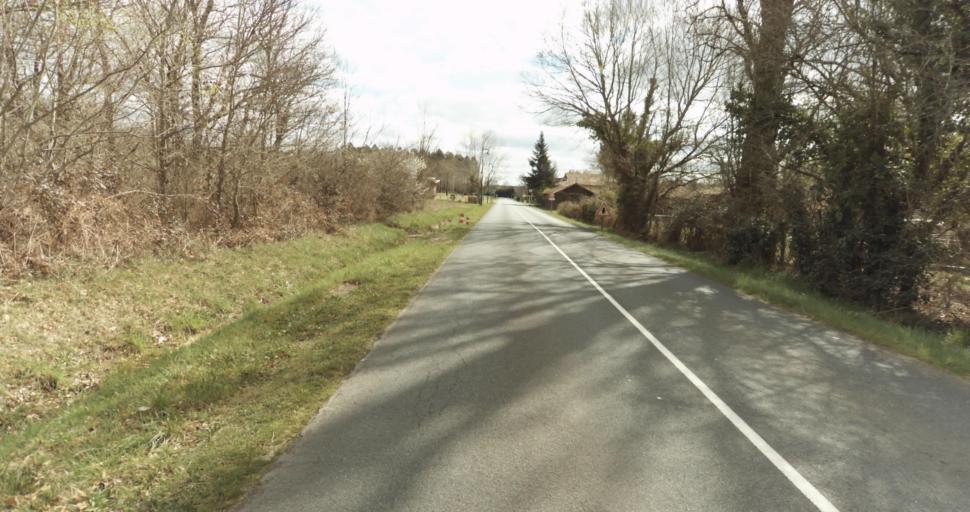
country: FR
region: Aquitaine
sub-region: Departement des Landes
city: Roquefort
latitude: 44.0721
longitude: -0.4299
